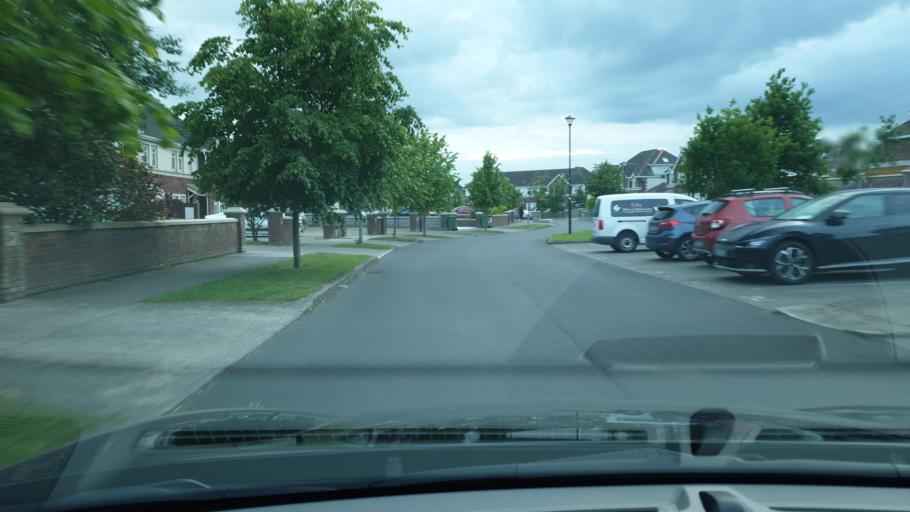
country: IE
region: Leinster
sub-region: An Mhi
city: Ashbourne
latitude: 53.5131
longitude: -6.3876
